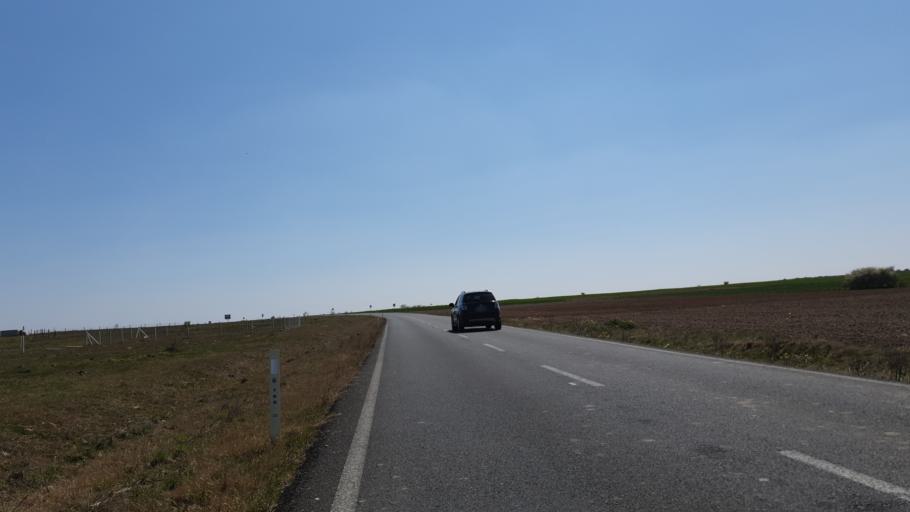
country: TR
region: Tekirdag
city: Velimese
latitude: 41.3284
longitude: 27.9203
